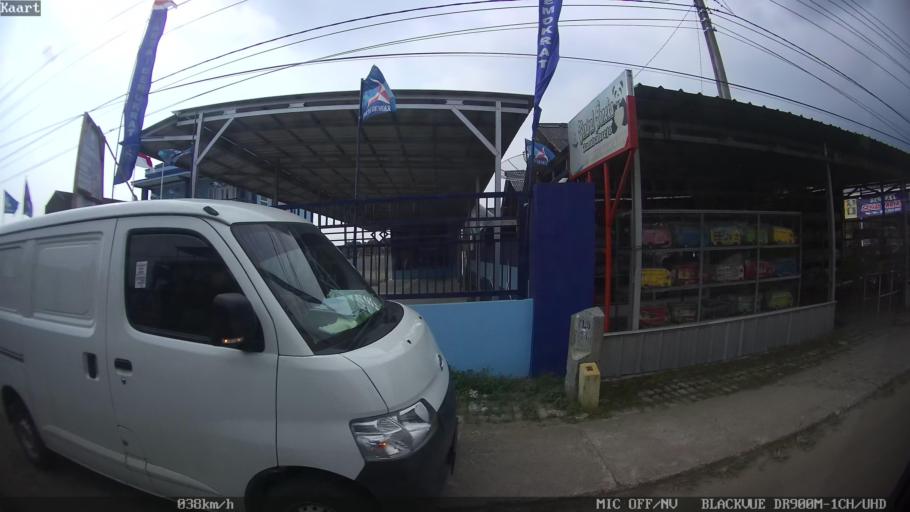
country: ID
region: Lampung
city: Gadingrejo
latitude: -5.3770
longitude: 105.0353
